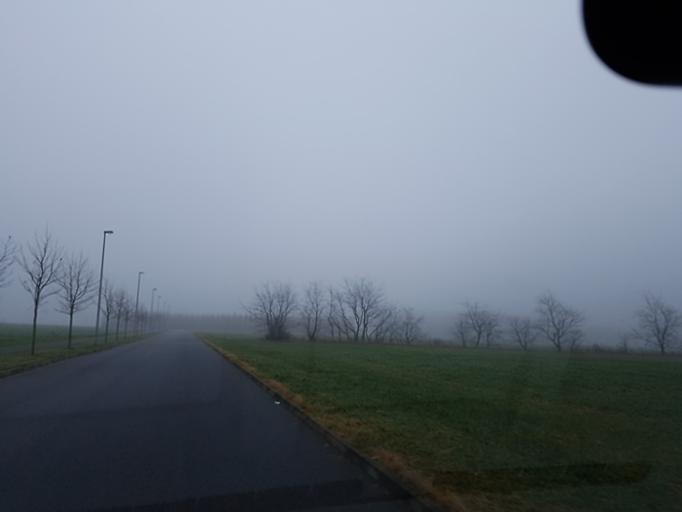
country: DE
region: Brandenburg
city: Finsterwalde
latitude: 51.6299
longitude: 13.7396
